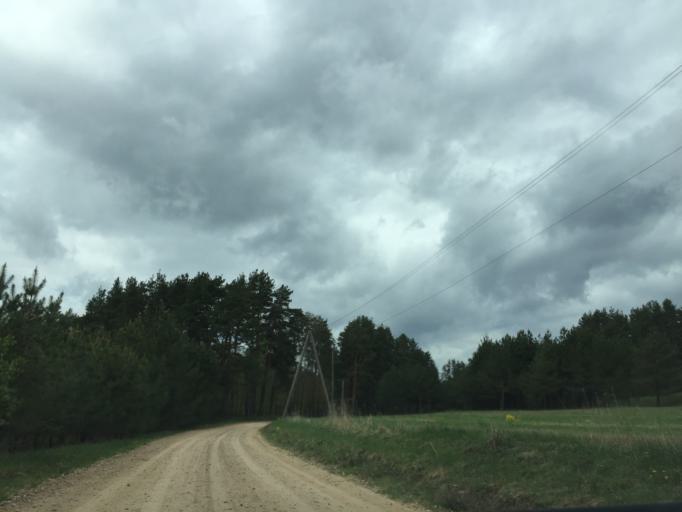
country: LV
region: Kekava
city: Kekava
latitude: 56.7939
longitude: 24.3095
